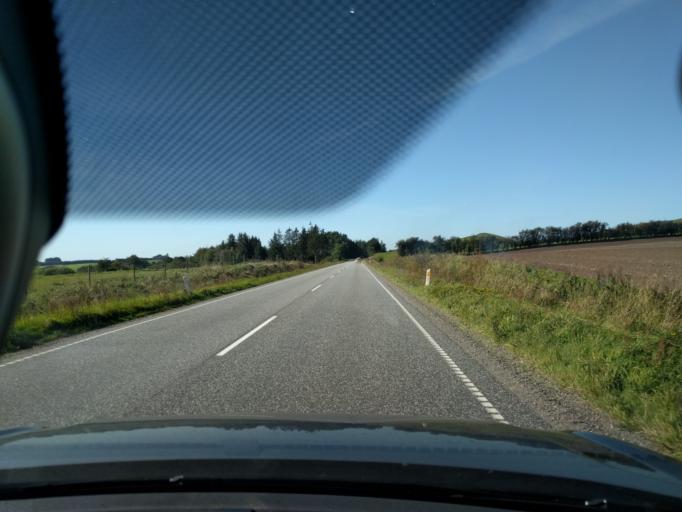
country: DK
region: North Denmark
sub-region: Mariagerfjord Kommune
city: Hobro
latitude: 56.6695
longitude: 9.7102
